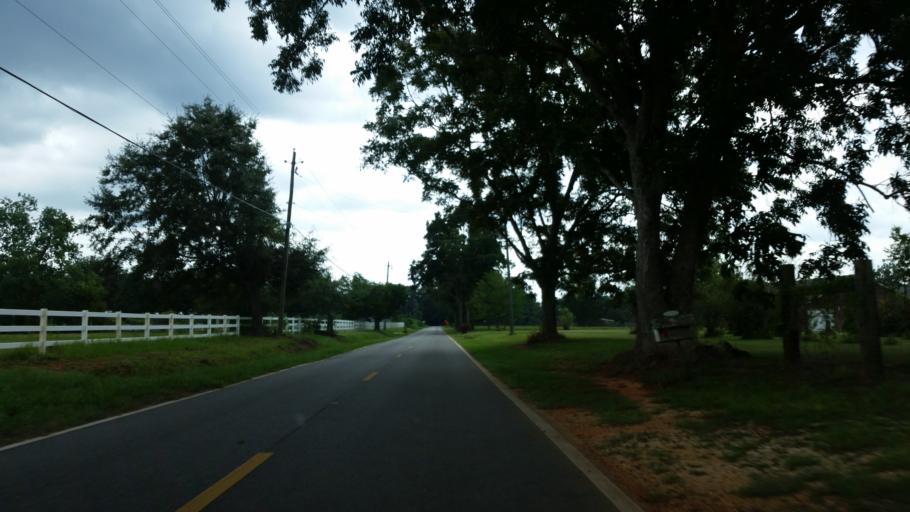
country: US
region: Florida
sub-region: Escambia County
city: Molino
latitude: 30.6949
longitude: -87.4055
